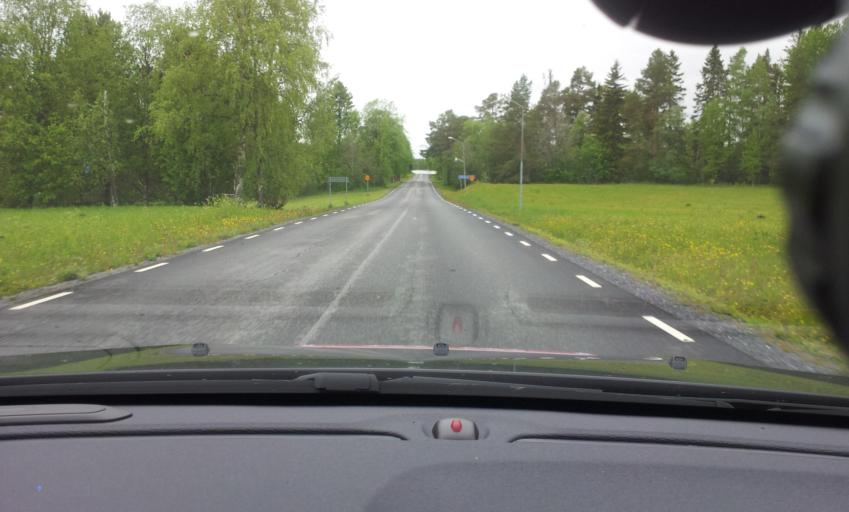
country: SE
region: Jaemtland
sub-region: Krokoms Kommun
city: Valla
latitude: 63.3267
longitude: 14.0332
